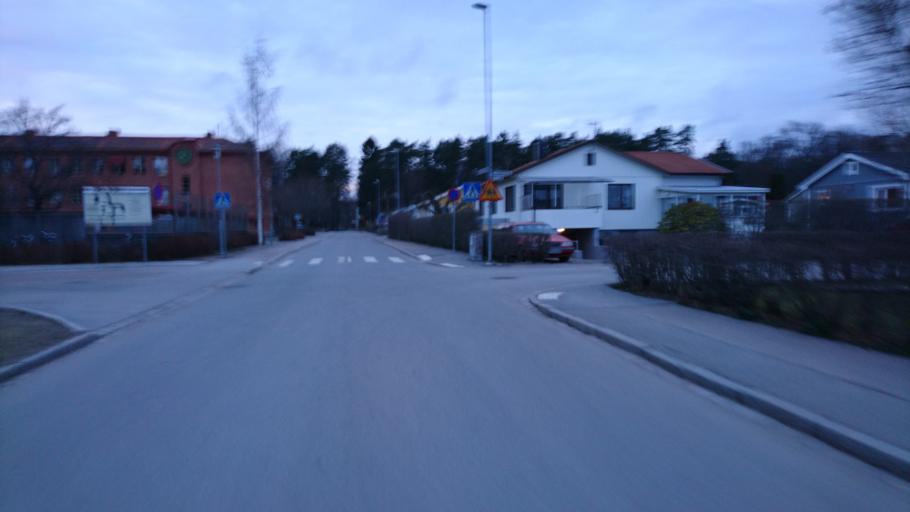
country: SE
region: Uppsala
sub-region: Uppsala Kommun
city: Uppsala
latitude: 59.8773
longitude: 17.6286
